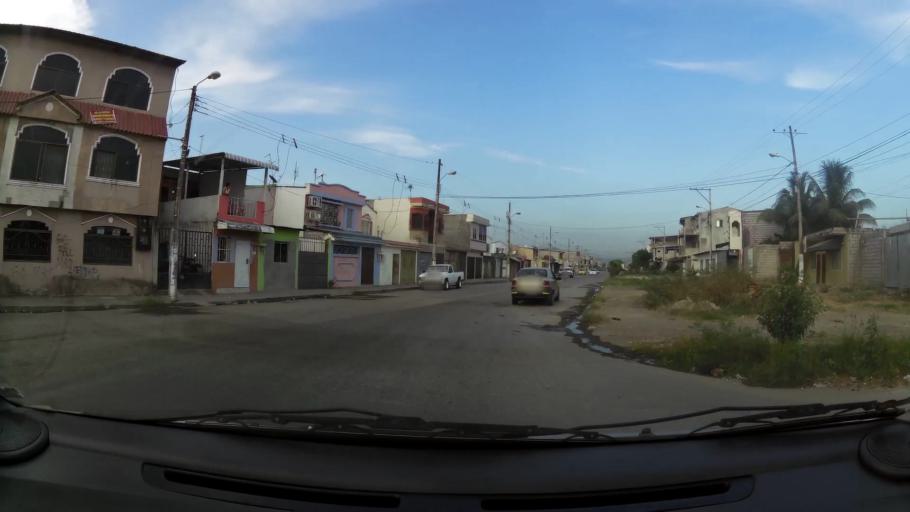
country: EC
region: Guayas
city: Eloy Alfaro
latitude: -2.0963
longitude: -79.9052
